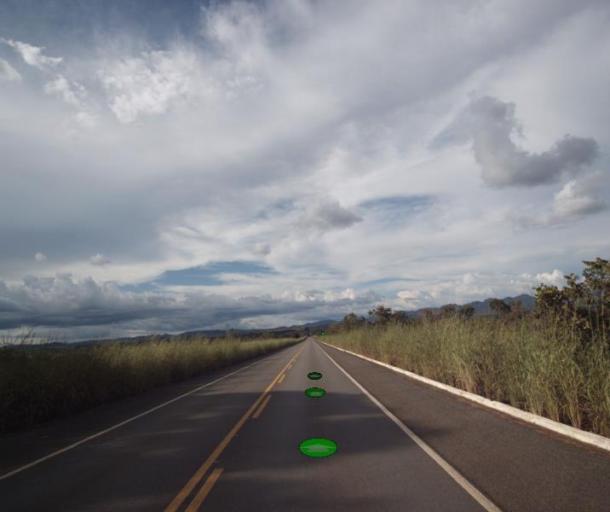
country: BR
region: Goias
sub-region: Niquelandia
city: Niquelandia
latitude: -14.7459
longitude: -48.6191
